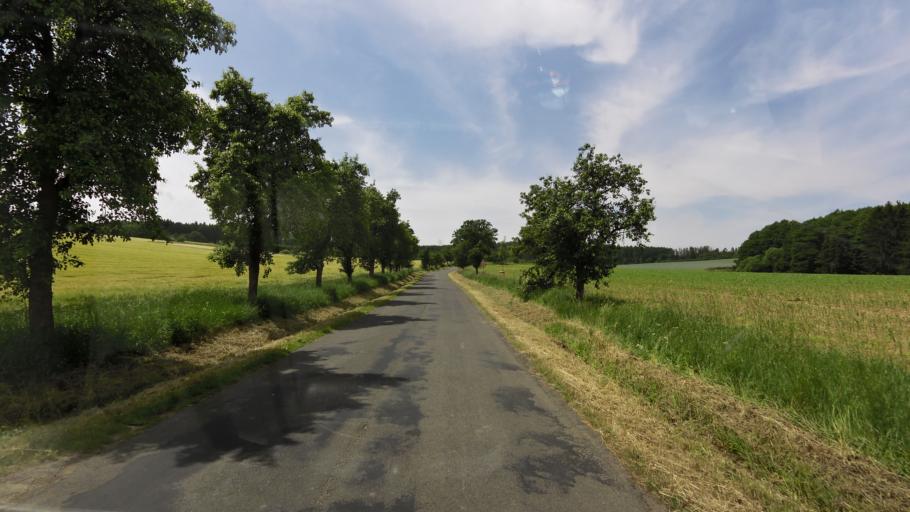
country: CZ
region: Plzensky
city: St'ahlavy
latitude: 49.6747
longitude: 13.4870
